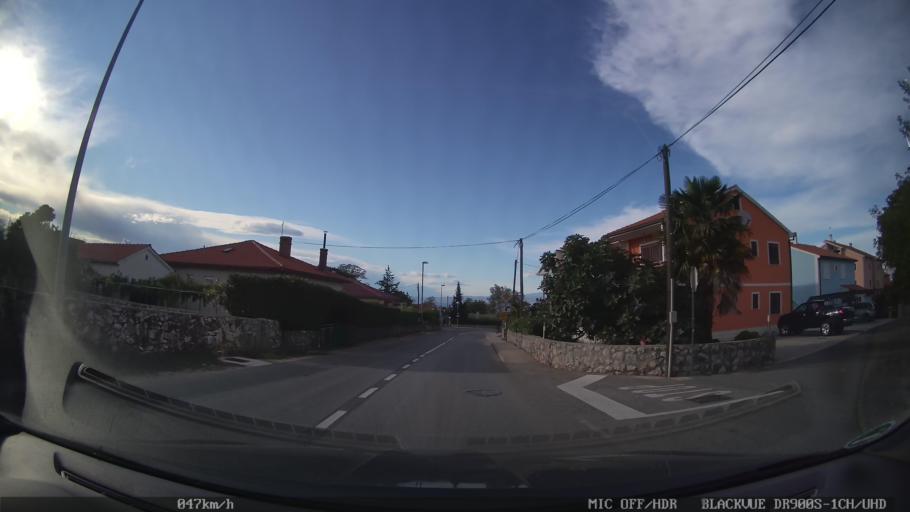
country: HR
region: Primorsko-Goranska
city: Njivice
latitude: 45.1143
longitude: 14.5237
